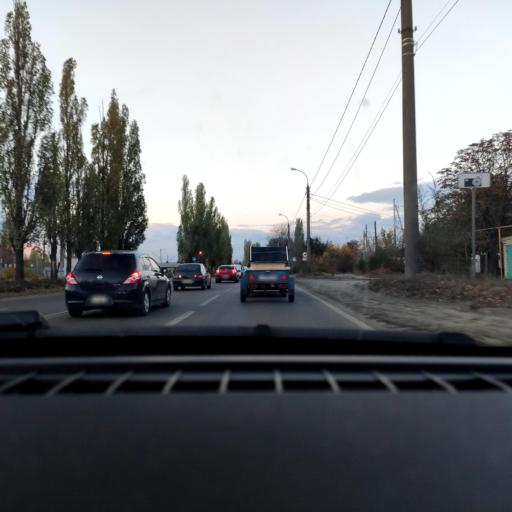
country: RU
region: Voronezj
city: Maslovka
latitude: 51.6162
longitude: 39.2584
